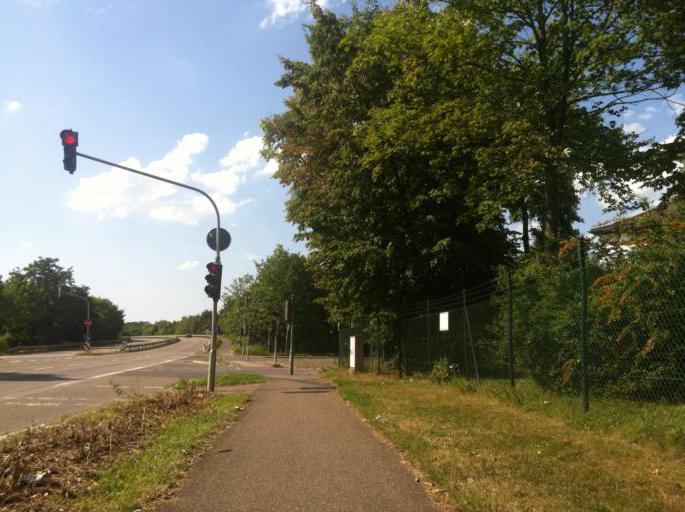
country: DE
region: North Rhine-Westphalia
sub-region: Regierungsbezirk Koln
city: Poll
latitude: 50.9051
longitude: 7.0191
